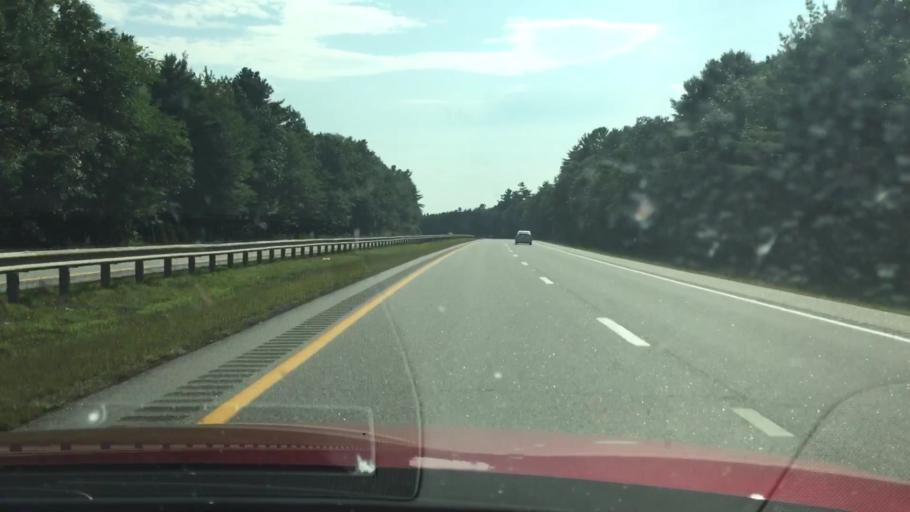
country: US
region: Maine
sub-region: Cumberland County
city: New Gloucester
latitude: 43.9767
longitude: -70.3163
